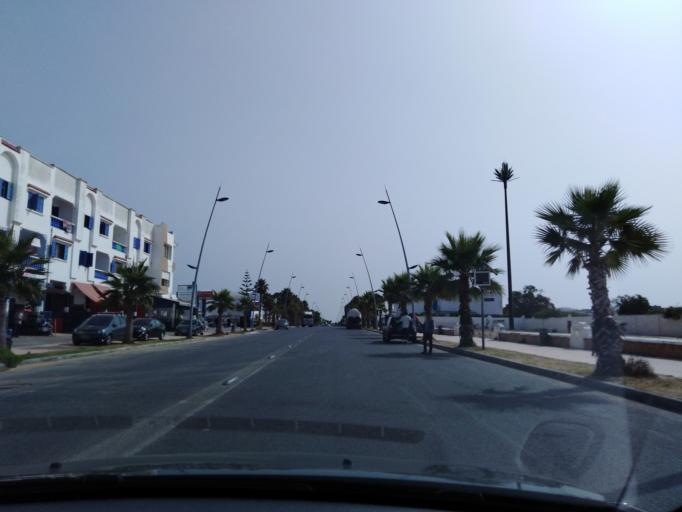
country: MA
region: Doukkala-Abda
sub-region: Safi
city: Safi
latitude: 32.7302
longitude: -9.0376
